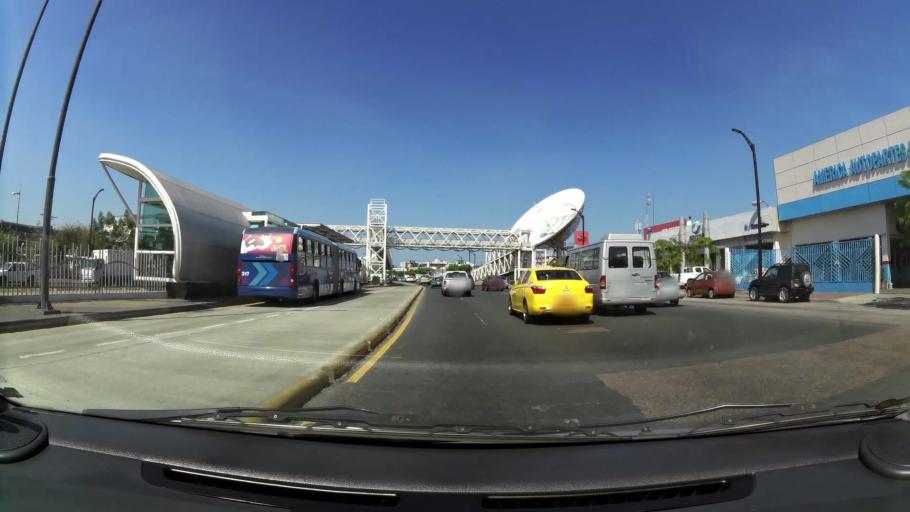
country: EC
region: Guayas
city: Eloy Alfaro
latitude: -2.1464
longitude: -79.8858
